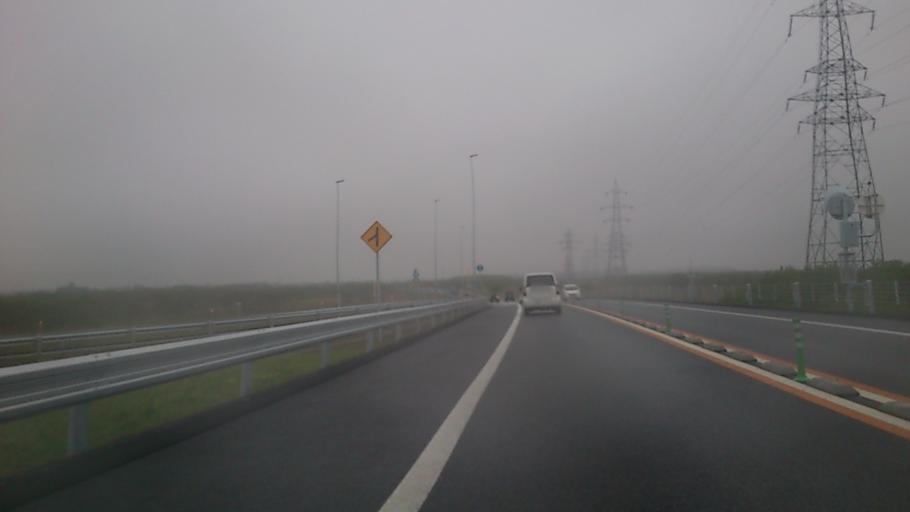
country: JP
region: Hokkaido
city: Kushiro
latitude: 43.0290
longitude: 144.4040
